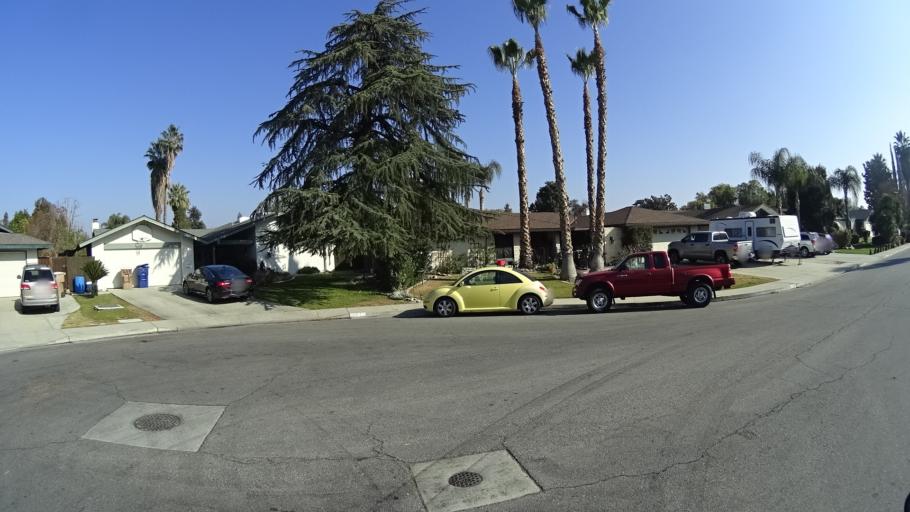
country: US
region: California
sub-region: Kern County
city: Greenacres
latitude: 35.3595
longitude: -119.0727
